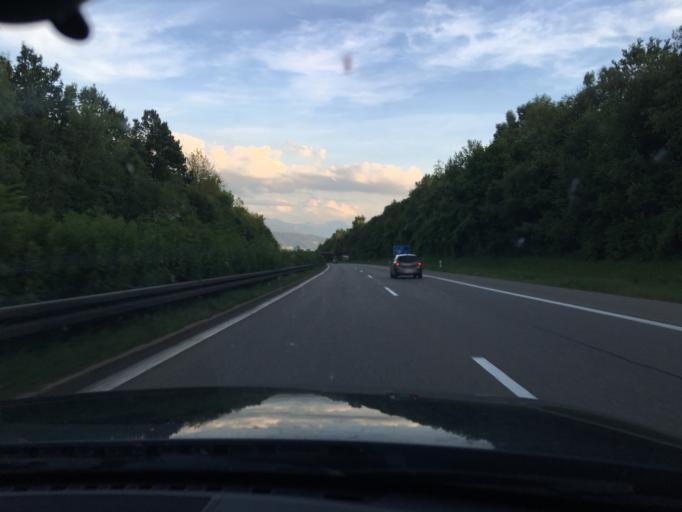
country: DE
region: Bavaria
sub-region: Swabia
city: Weissensberg
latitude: 47.5745
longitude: 9.7348
